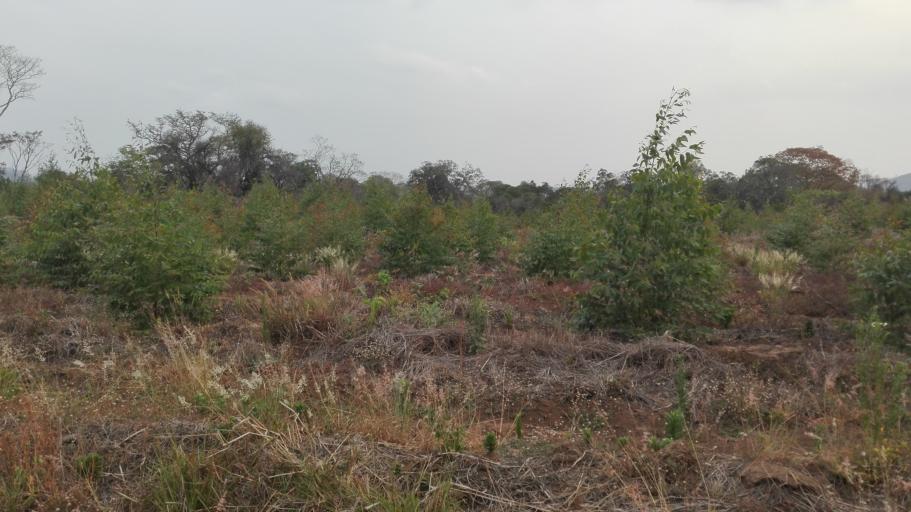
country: MZ
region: Nampula
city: Mutuali
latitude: -15.6352
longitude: 36.9349
